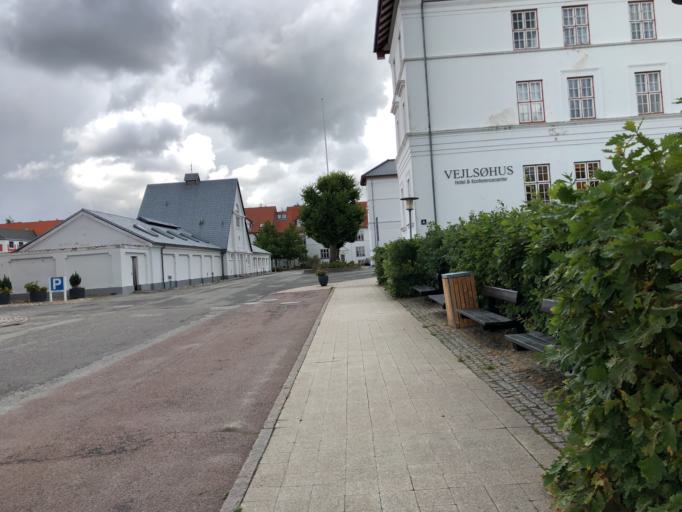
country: DK
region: Central Jutland
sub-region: Silkeborg Kommune
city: Silkeborg
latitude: 56.1537
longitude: 9.5597
